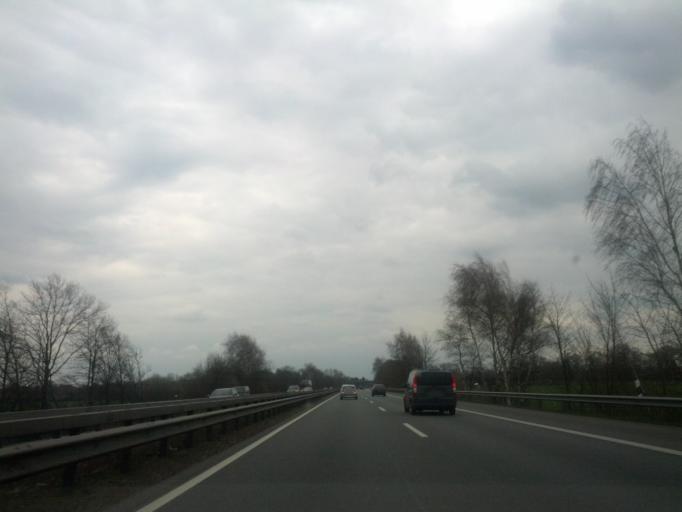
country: DE
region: Lower Saxony
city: Hatten
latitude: 53.0846
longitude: 8.3084
